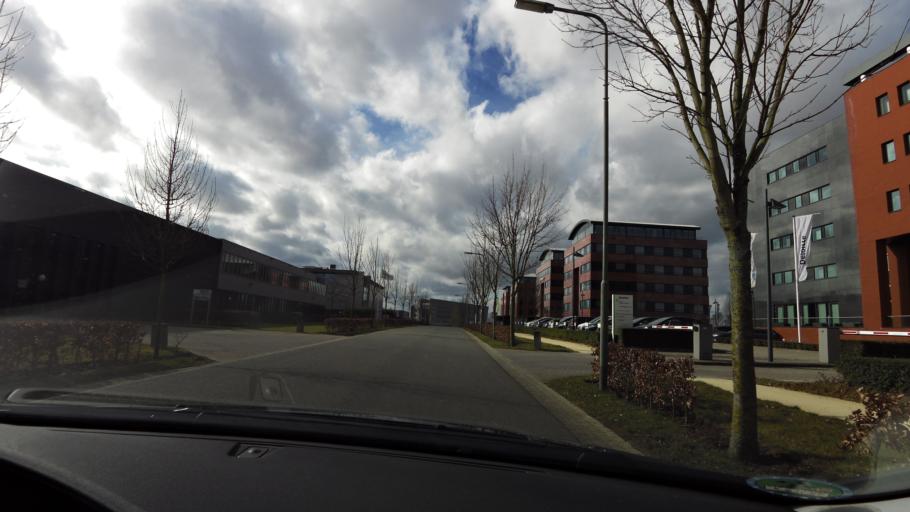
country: NL
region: Limburg
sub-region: Gemeente Beek
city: Beek
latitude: 50.9311
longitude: 5.7818
